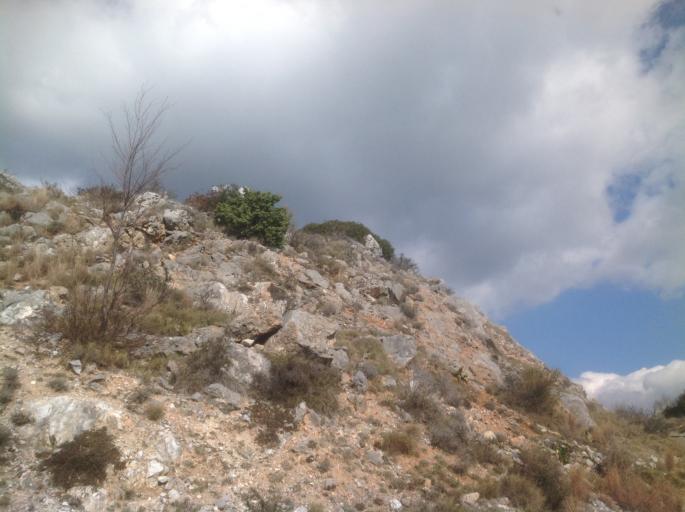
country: IT
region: Calabria
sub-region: Provincia di Cosenza
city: Civita
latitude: 39.8281
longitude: 16.3069
